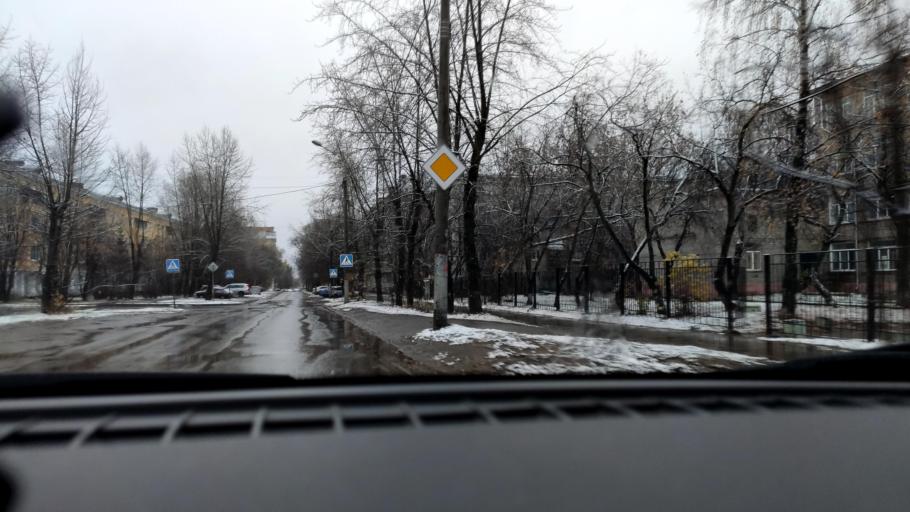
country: RU
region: Perm
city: Kultayevo
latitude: 57.9957
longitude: 55.9407
